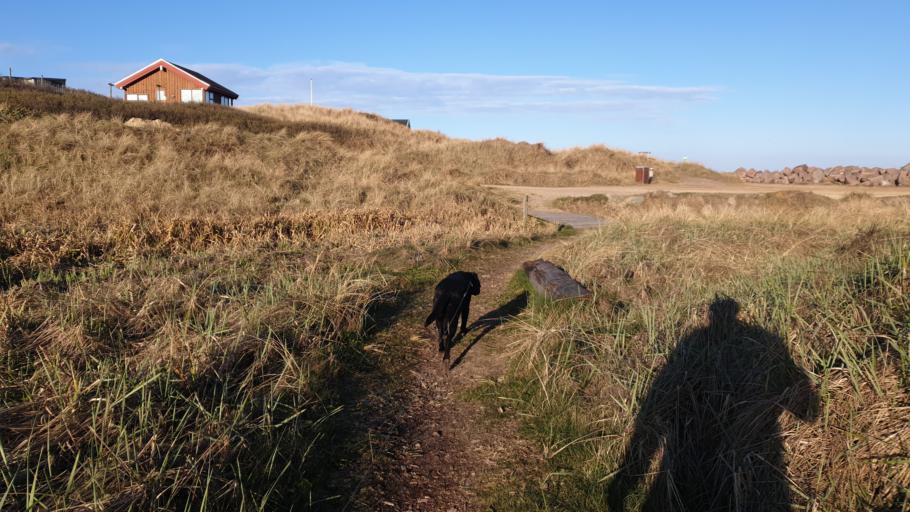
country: DK
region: North Denmark
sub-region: Hjorring Kommune
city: Hjorring
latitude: 57.4856
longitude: 9.8120
